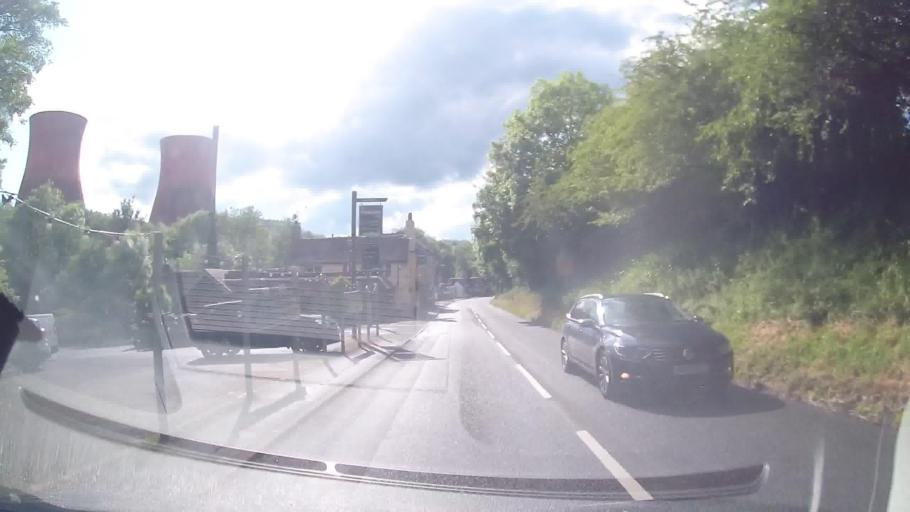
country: GB
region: England
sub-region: Telford and Wrekin
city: Ironbridge
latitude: 52.6321
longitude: -2.5017
